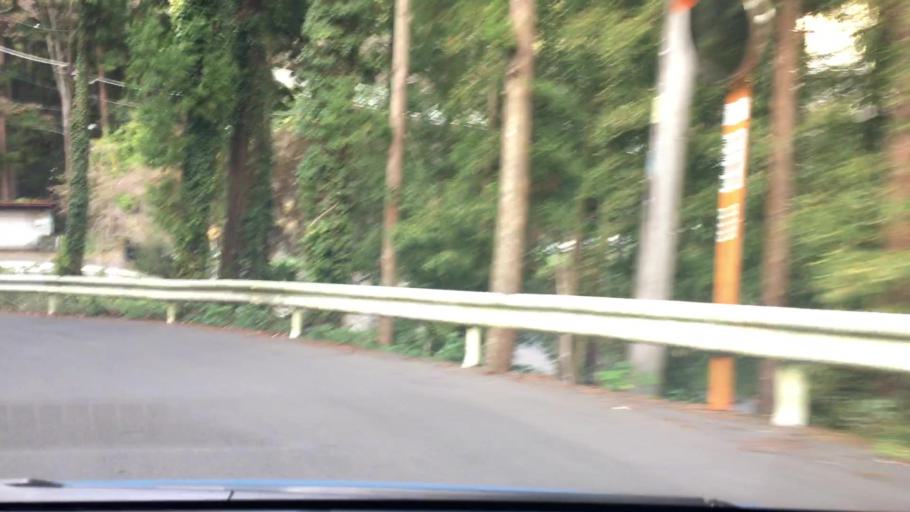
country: JP
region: Yamanashi
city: Uenohara
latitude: 35.5602
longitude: 139.1659
